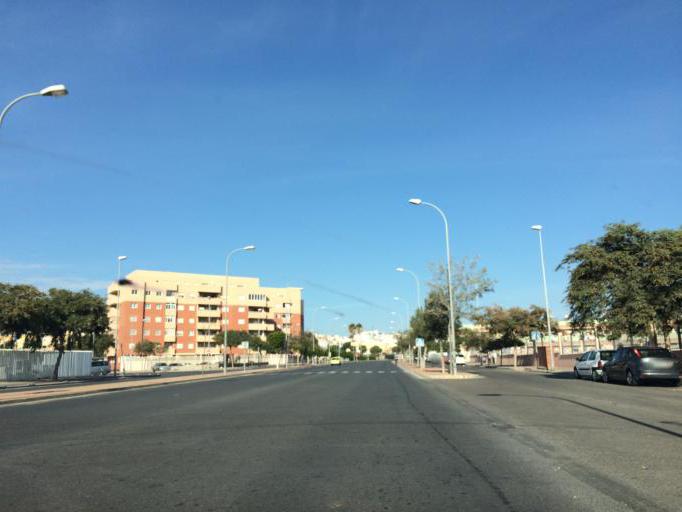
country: ES
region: Andalusia
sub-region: Provincia de Almeria
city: Almeria
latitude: 36.8452
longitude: -2.4333
